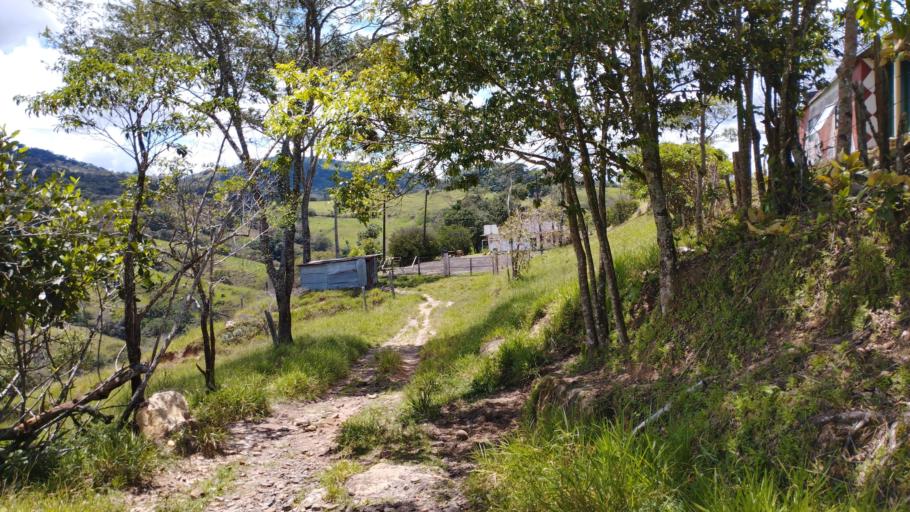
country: CO
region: Boyaca
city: San Luis de Gaceno
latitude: 4.7753
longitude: -73.1311
